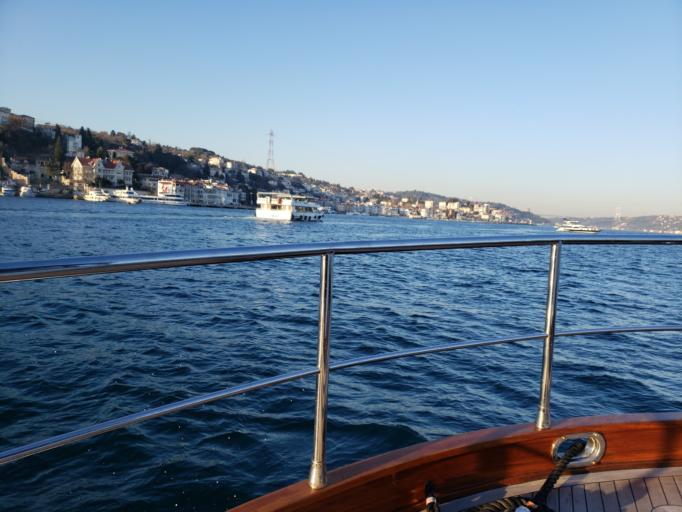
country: TR
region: Istanbul
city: UEskuedar
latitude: 41.0593
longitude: 29.0414
